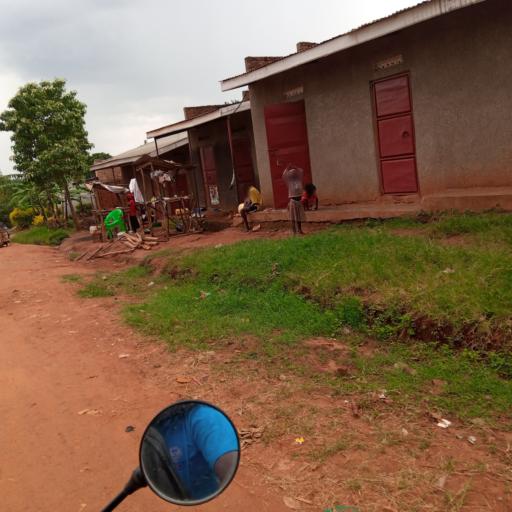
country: UG
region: Eastern Region
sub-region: Mbale District
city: Mbale
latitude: 1.1263
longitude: 34.1778
